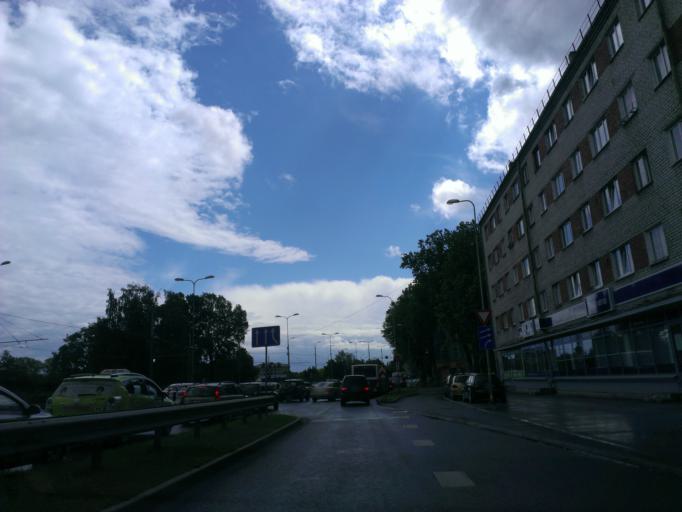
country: LV
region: Riga
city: Riga
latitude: 56.9463
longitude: 24.0826
